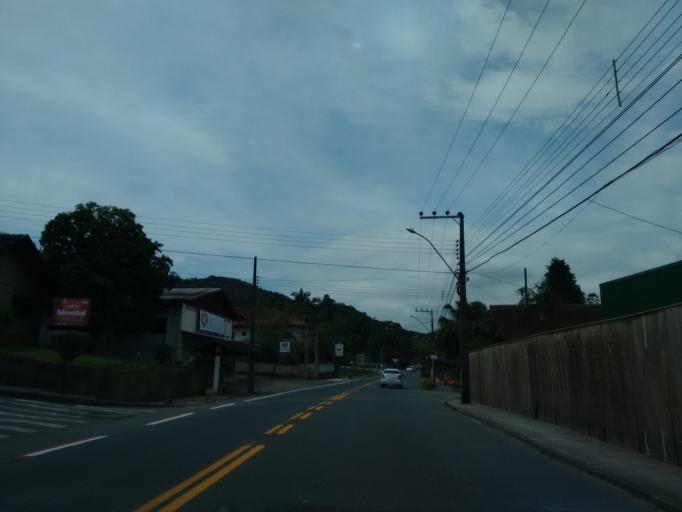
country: BR
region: Santa Catarina
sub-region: Pomerode
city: Pomerode
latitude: -26.7188
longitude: -49.1677
